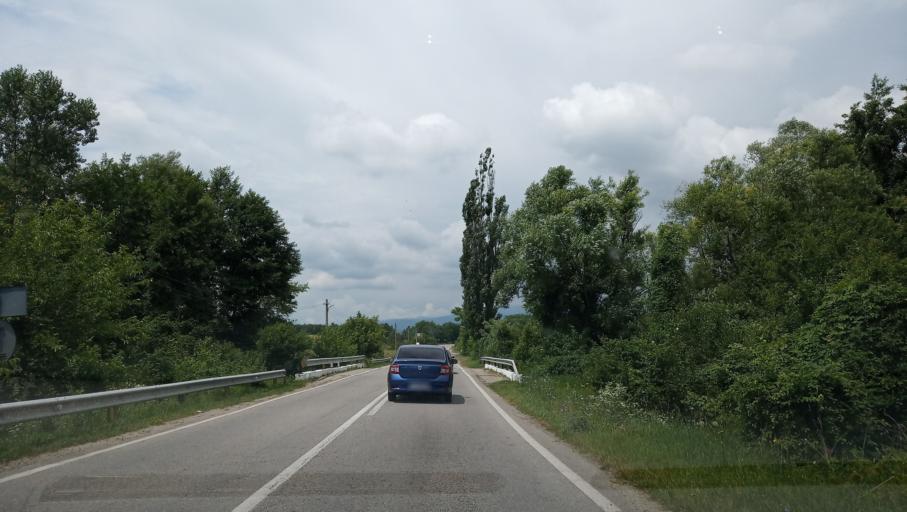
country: RO
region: Gorj
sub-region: Comuna Lelesti
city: Lelesti
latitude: 45.0819
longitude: 23.1712
